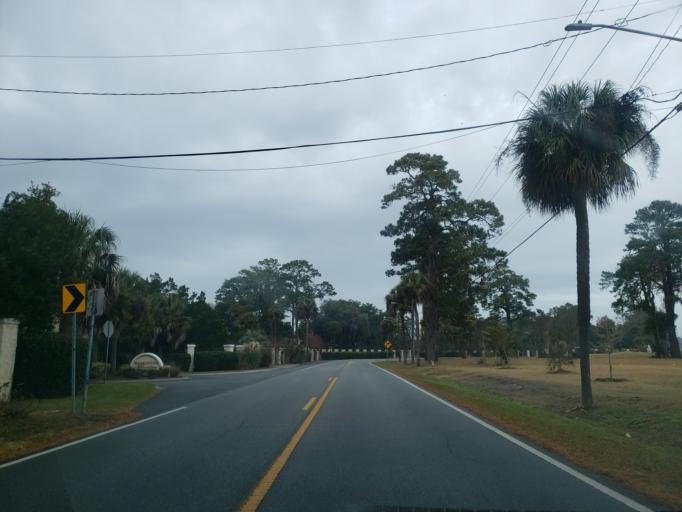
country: US
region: Georgia
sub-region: Chatham County
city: Wilmington Island
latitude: 32.0035
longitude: -80.9983
